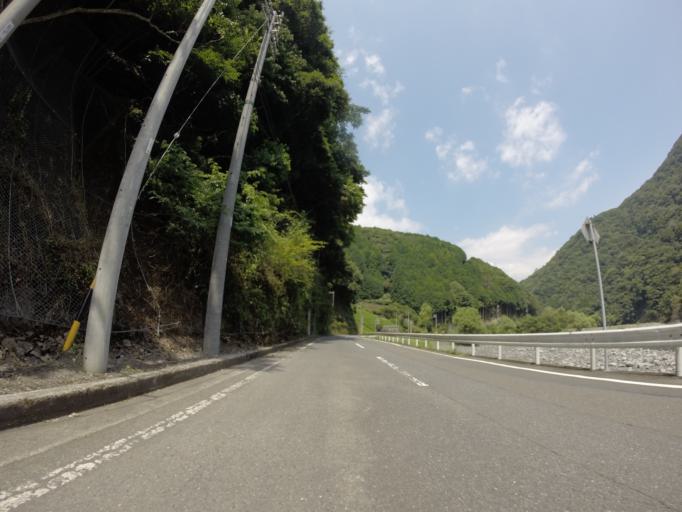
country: JP
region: Shizuoka
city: Shizuoka-shi
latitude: 35.2146
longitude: 138.3513
